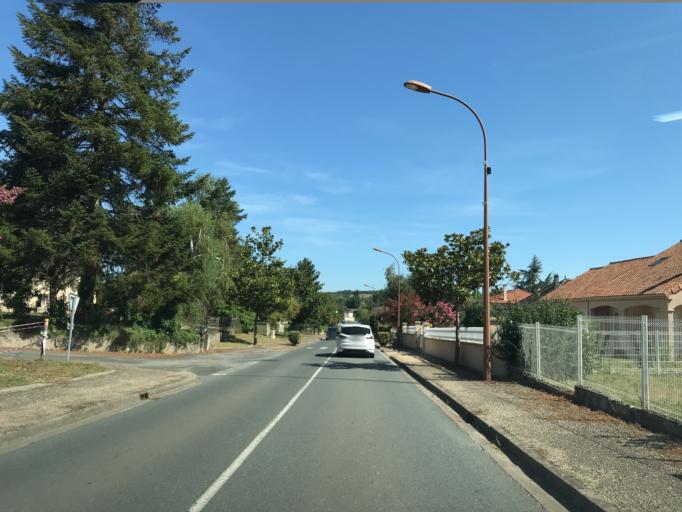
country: FR
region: Limousin
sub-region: Departement de la Correze
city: Larche
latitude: 45.1202
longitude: 1.4109
